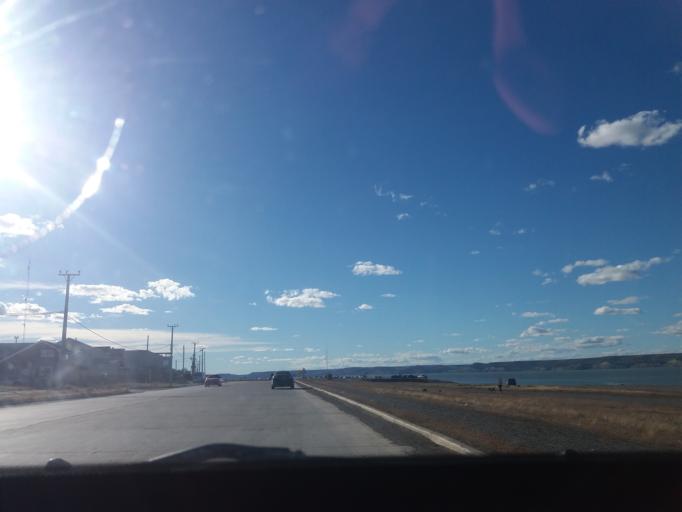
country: AR
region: Santa Cruz
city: Rio Gallegos
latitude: -51.6037
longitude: -69.2471
